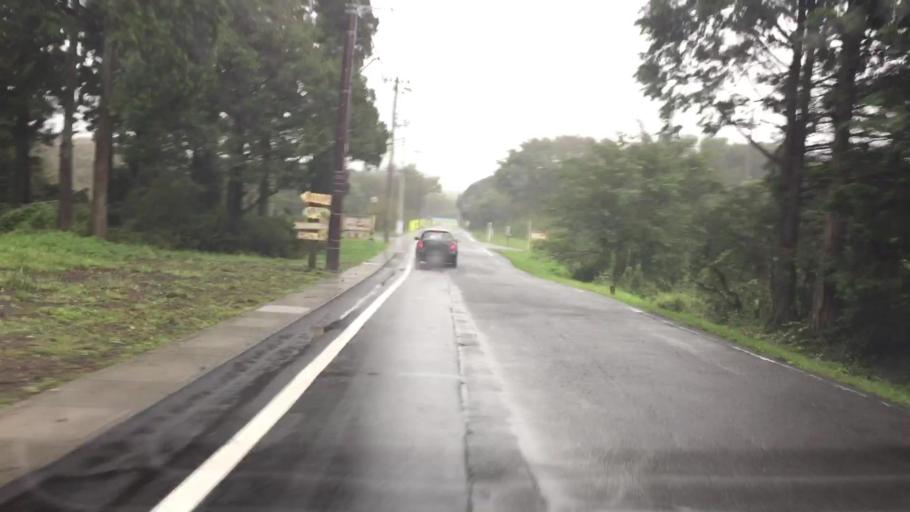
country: JP
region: Yamanashi
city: Fujikawaguchiko
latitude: 35.3908
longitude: 138.6069
